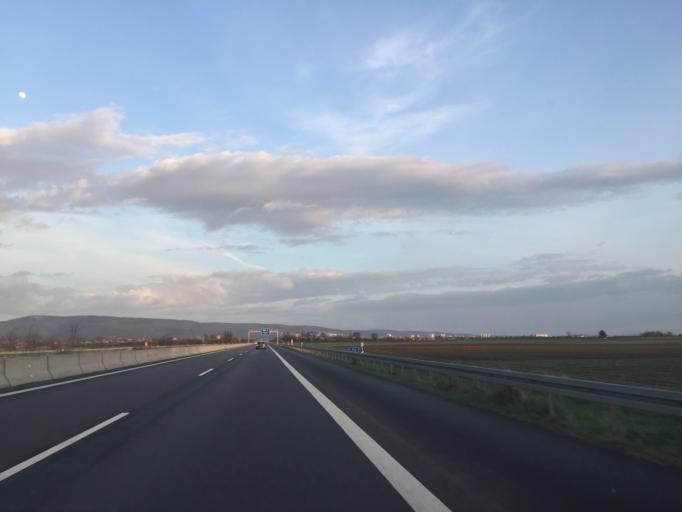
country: DE
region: Baden-Wuerttemberg
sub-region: Karlsruhe Region
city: Edingen-Neckarhausen
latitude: 49.4362
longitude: 8.6021
